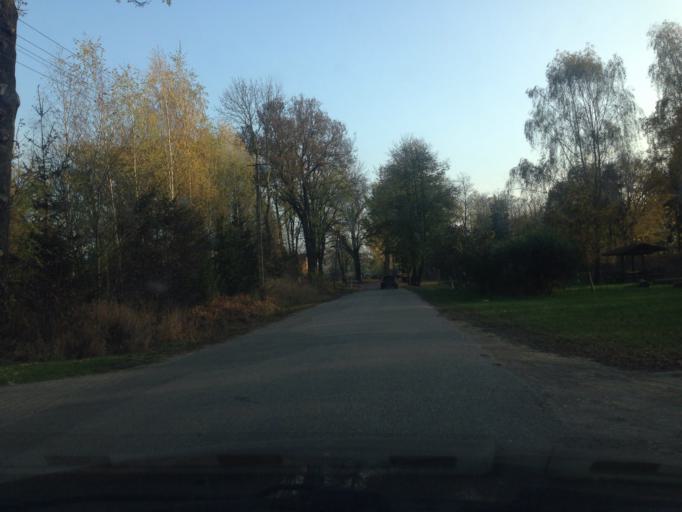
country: PL
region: Kujawsko-Pomorskie
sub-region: Powiat wabrzeski
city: Debowa Laka
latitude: 53.2577
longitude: 19.0923
